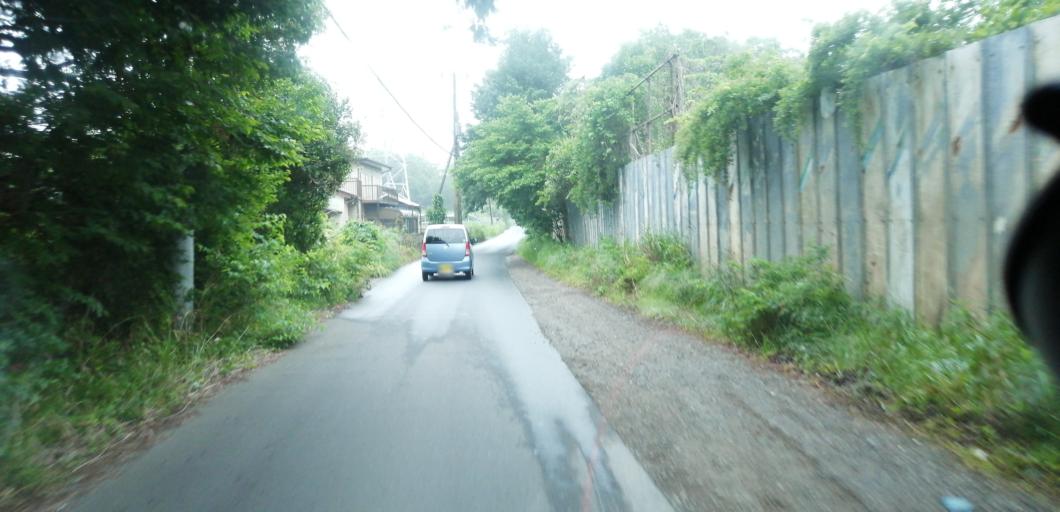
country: JP
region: Chiba
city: Ichihara
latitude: 35.4805
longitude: 140.1487
